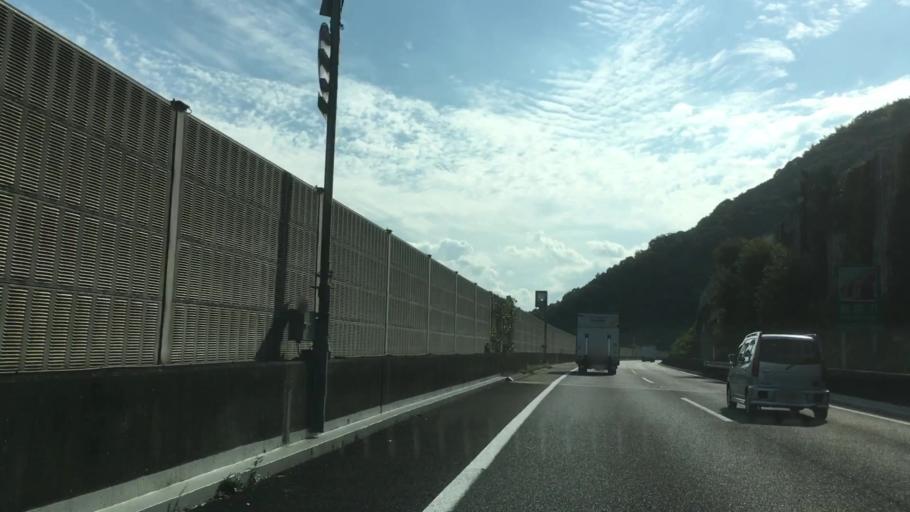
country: JP
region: Yamaguchi
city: Otake
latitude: 34.2214
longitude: 132.2001
